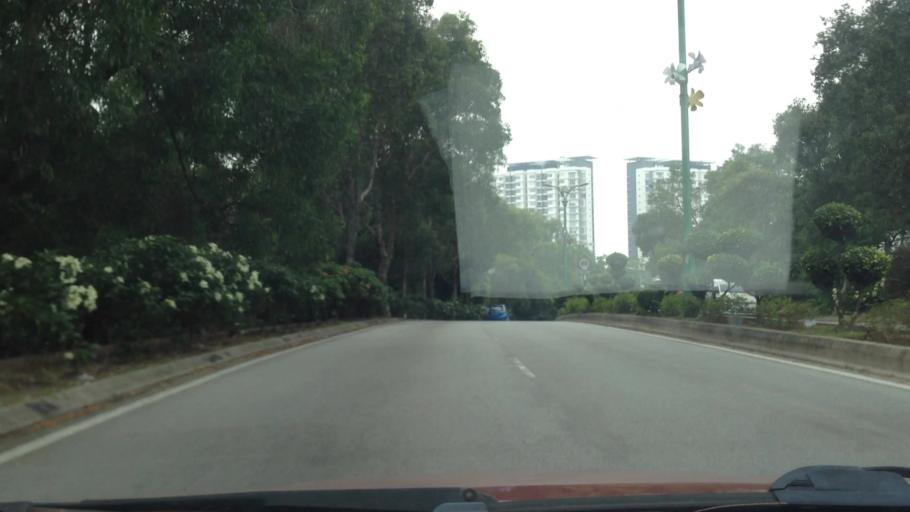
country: MY
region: Selangor
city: Shah Alam
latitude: 3.0733
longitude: 101.5360
